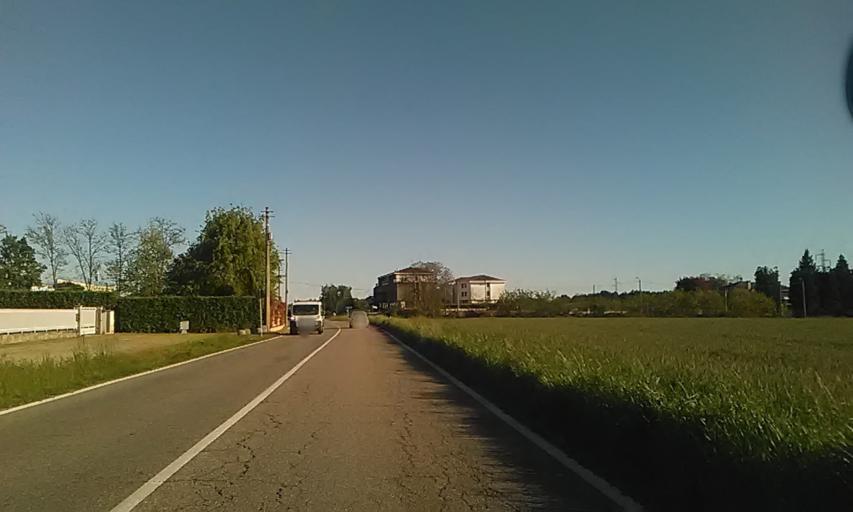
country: IT
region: Piedmont
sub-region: Provincia di Novara
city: Cavaglietto
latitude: 45.6104
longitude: 8.5215
